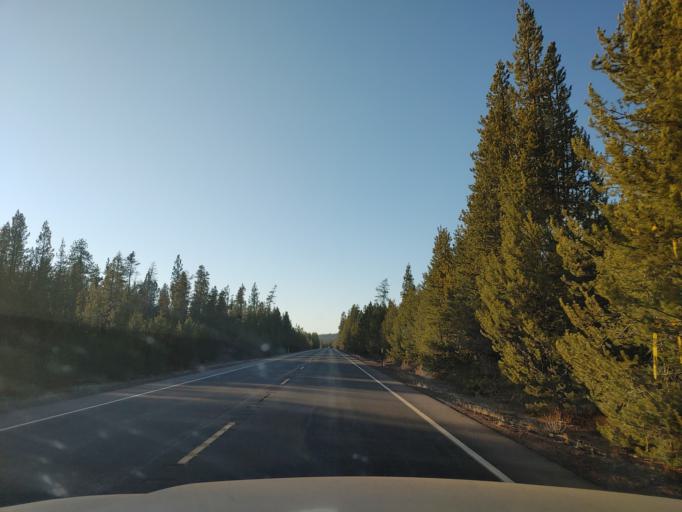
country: US
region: Oregon
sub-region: Deschutes County
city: La Pine
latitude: 43.4115
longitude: -121.8321
